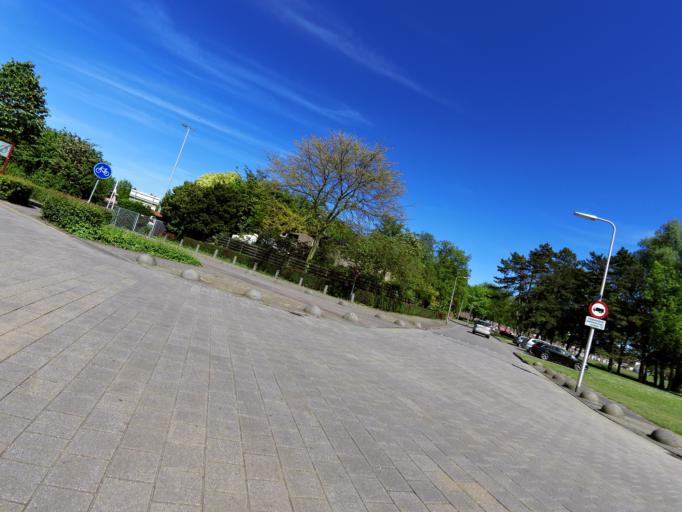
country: NL
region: South Holland
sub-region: Gemeente Hellevoetsluis
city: Hellevoetsluis
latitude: 51.8299
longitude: 4.1309
